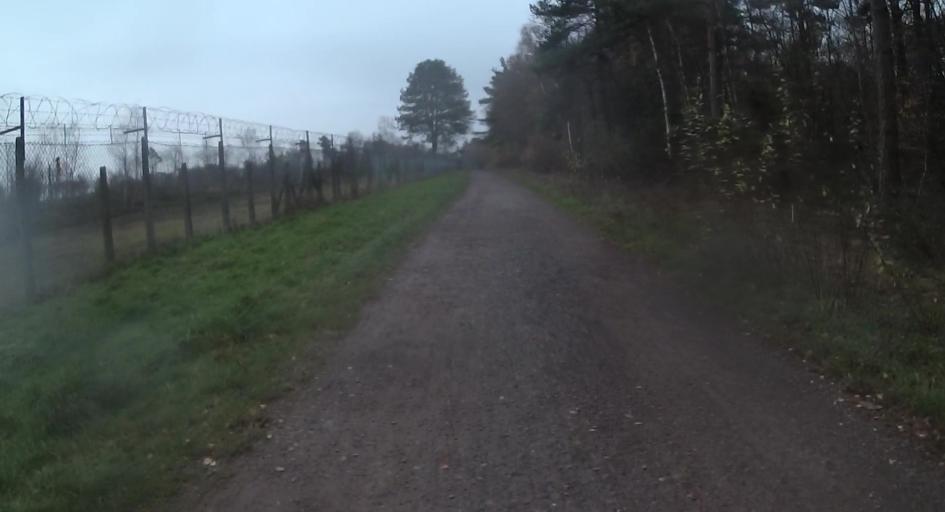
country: GB
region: England
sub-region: Surrey
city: Bagshot
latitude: 51.3352
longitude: -0.6980
